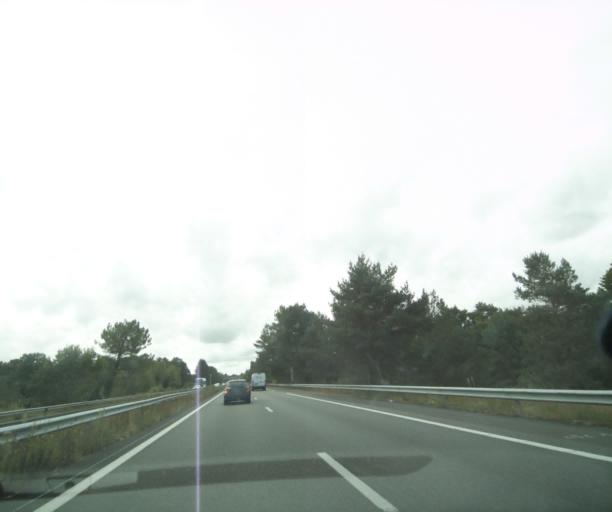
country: FR
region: Poitou-Charentes
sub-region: Departement de la Charente-Maritime
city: Saint-Genis-de-Saintonge
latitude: 45.4520
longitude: -0.6138
